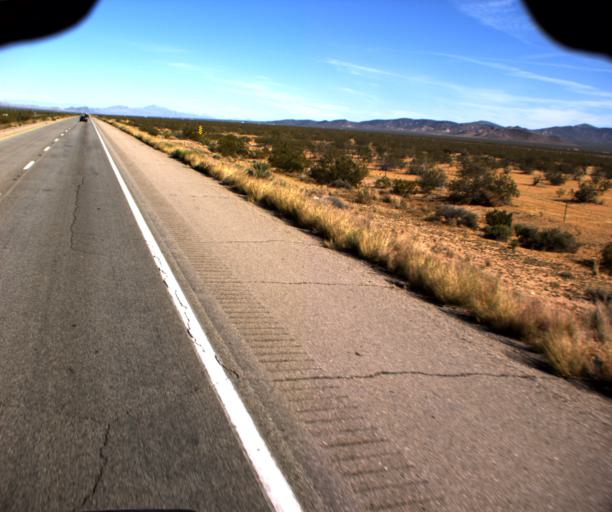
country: US
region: Arizona
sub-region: Mohave County
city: Dolan Springs
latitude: 35.5656
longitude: -114.3771
